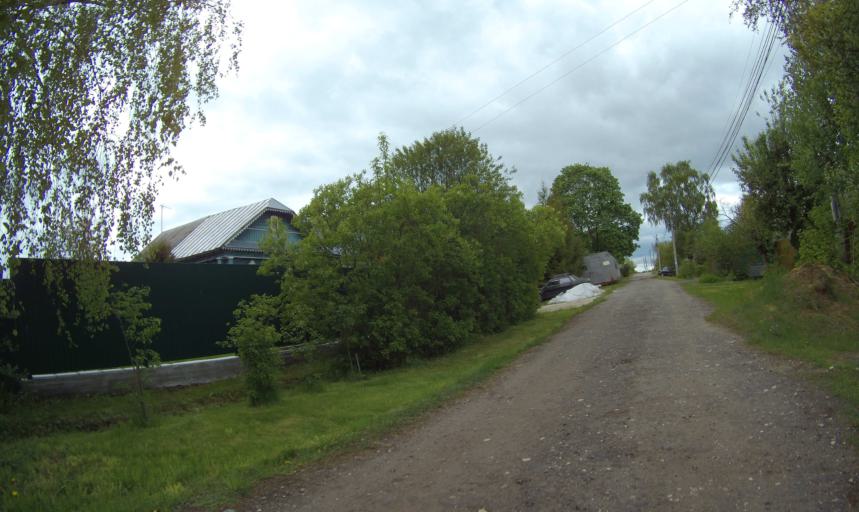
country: RU
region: Moskovskaya
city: Rechitsy
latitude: 55.5751
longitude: 38.5010
